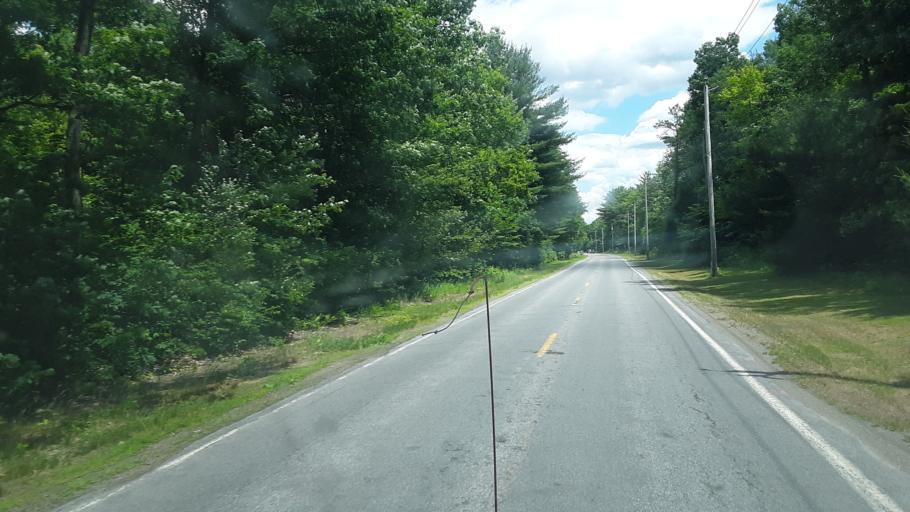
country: US
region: New York
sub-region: Oneida County
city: Rome
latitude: 43.2631
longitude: -75.5726
